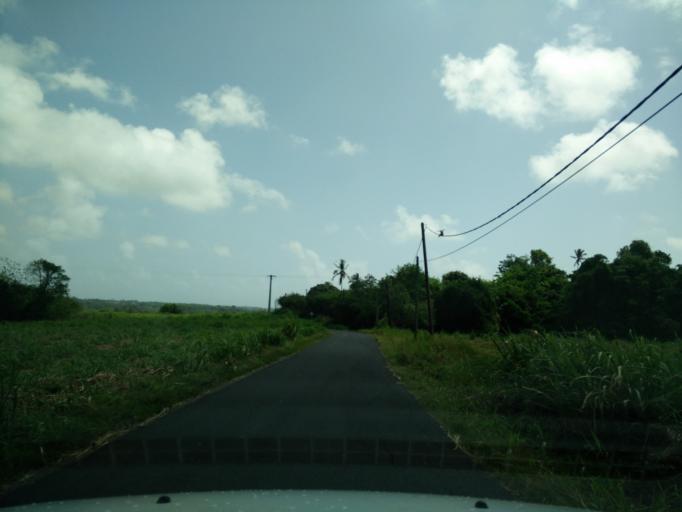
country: GP
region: Guadeloupe
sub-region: Guadeloupe
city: Grand-Bourg
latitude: 15.9158
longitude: -61.2731
